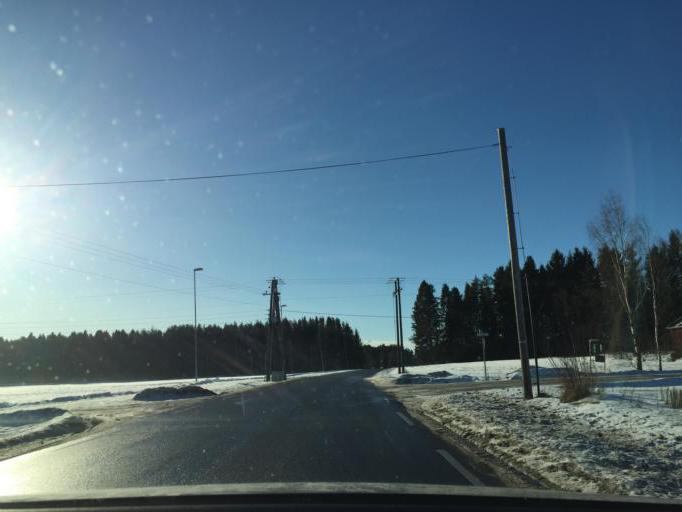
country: NO
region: Akershus
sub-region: Nes
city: Fjellfoten
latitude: 60.0977
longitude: 11.4826
